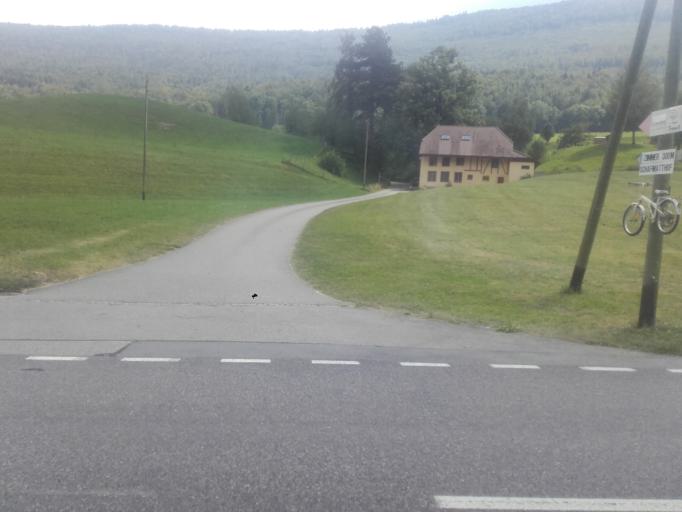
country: CH
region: Solothurn
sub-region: Bezirk Thal
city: Welschenrohr
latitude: 47.2675
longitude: 7.4866
